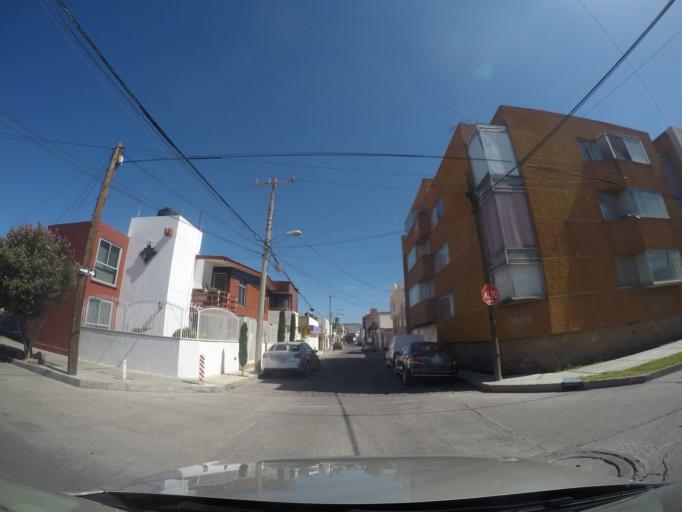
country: MX
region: San Luis Potosi
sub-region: San Luis Potosi
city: San Luis Potosi
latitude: 22.1507
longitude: -101.0087
